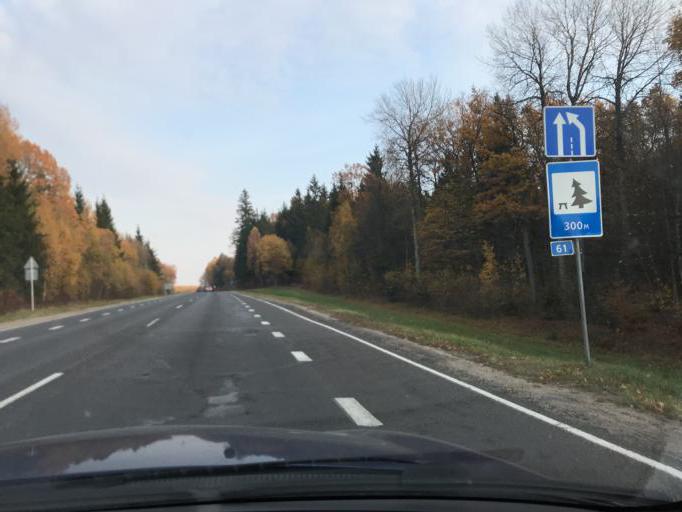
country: BY
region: Grodnenskaya
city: Navahrudak
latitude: 53.5892
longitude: 25.8896
